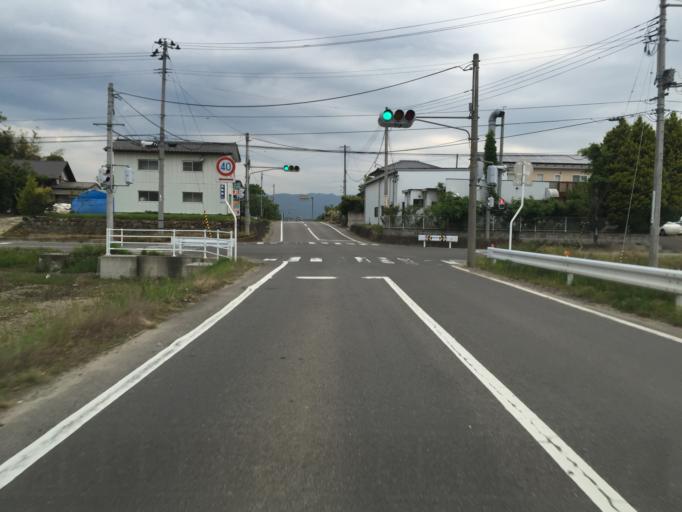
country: JP
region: Fukushima
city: Hobaramachi
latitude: 37.8258
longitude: 140.5360
